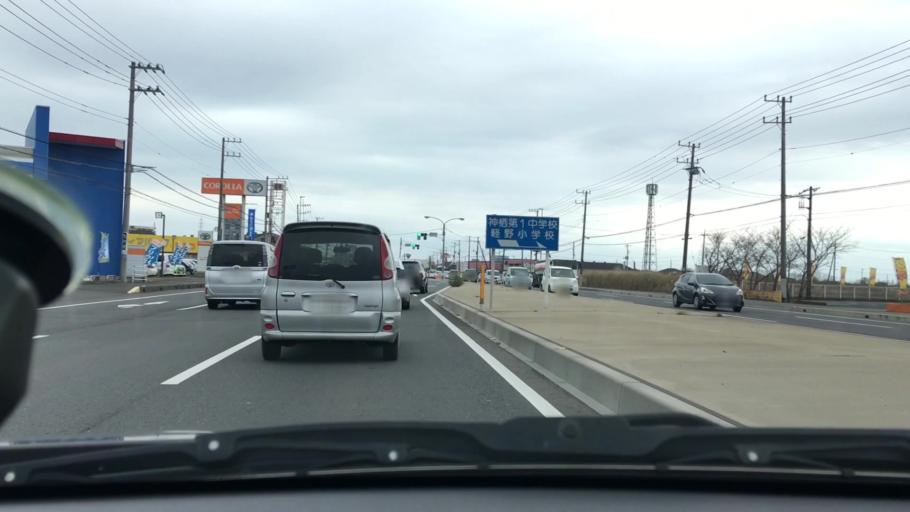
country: JP
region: Chiba
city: Omigawa
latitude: 35.8853
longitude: 140.6739
